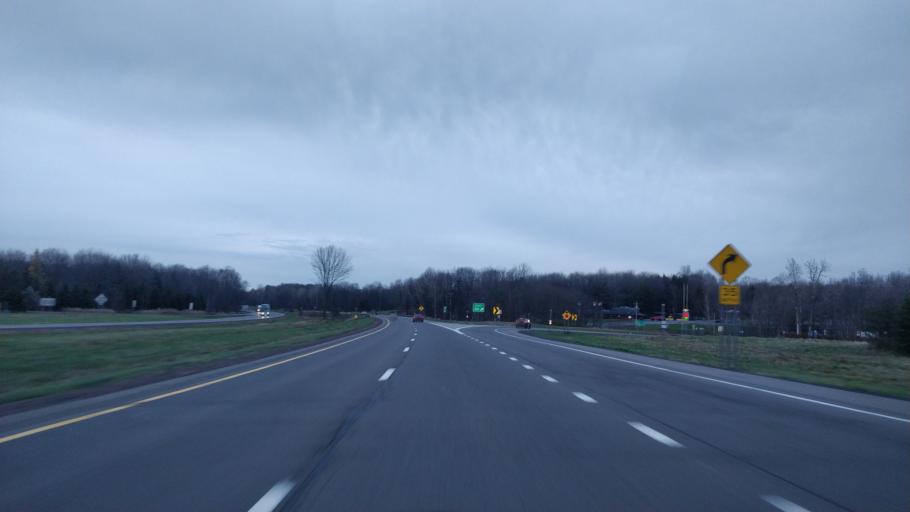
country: US
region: New York
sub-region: Oswego County
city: Central Square
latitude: 43.4049
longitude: -76.1165
